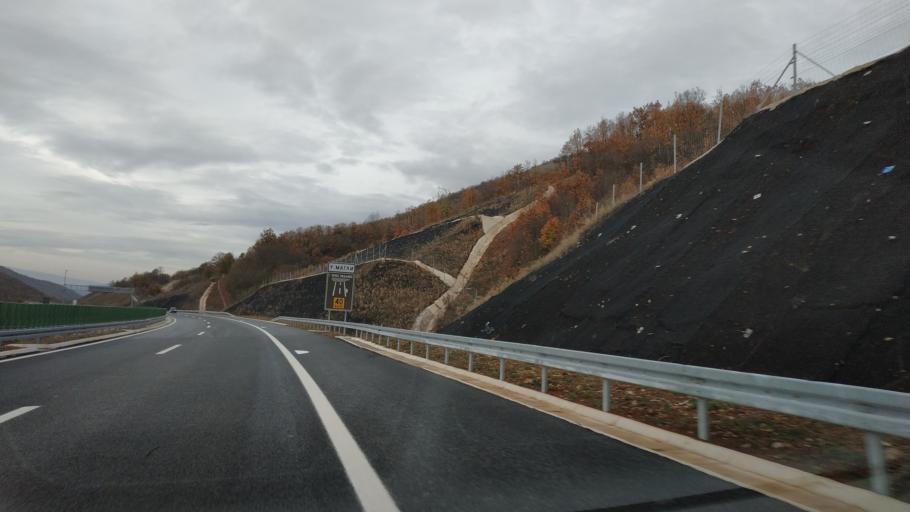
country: RS
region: Central Serbia
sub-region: Nisavski Okrug
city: Gadzin Han
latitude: 43.2806
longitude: 22.1348
